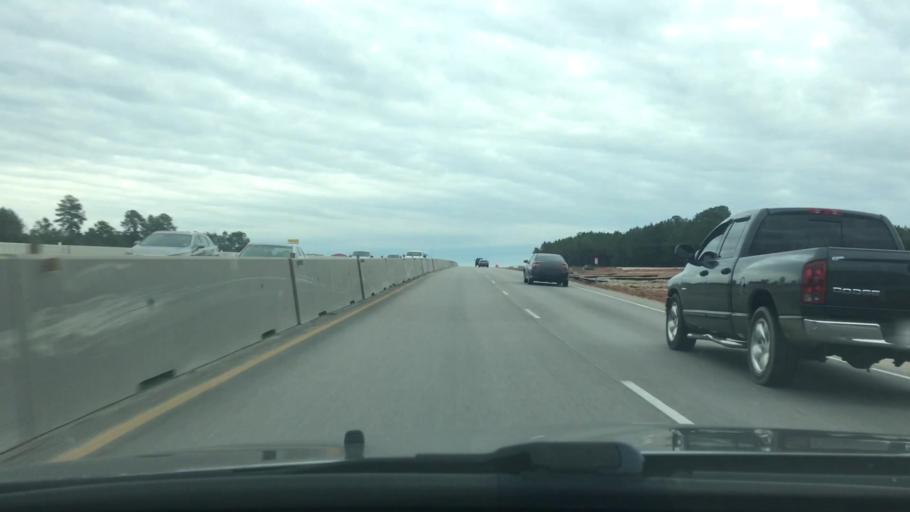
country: US
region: Texas
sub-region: Walker County
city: Huntsville
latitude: 30.6799
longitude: -95.5258
